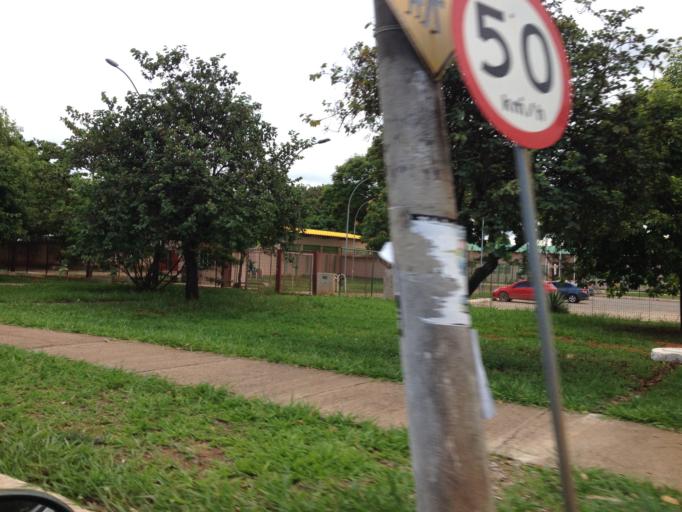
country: BR
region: Federal District
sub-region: Brasilia
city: Brasilia
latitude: -15.7832
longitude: -47.9377
